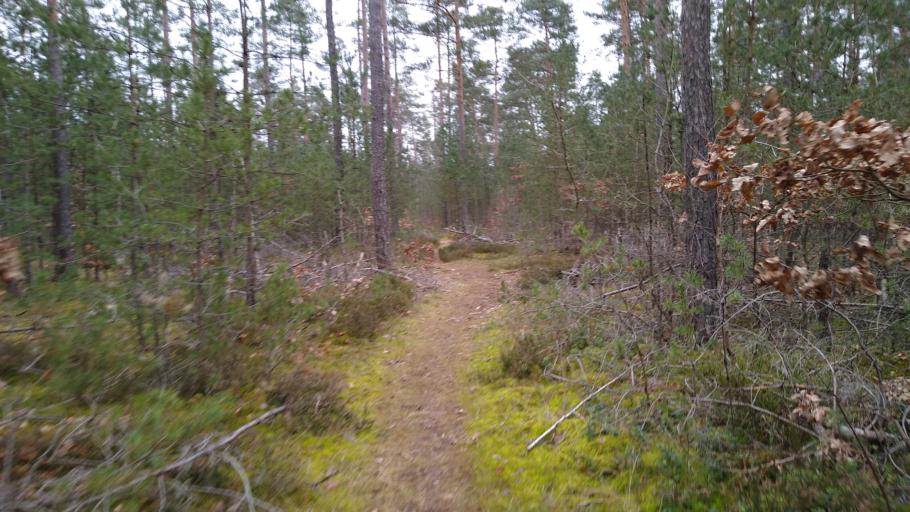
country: DE
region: Bavaria
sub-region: Regierungsbezirk Mittelfranken
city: Heroldsberg
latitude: 49.4900
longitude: 11.1368
